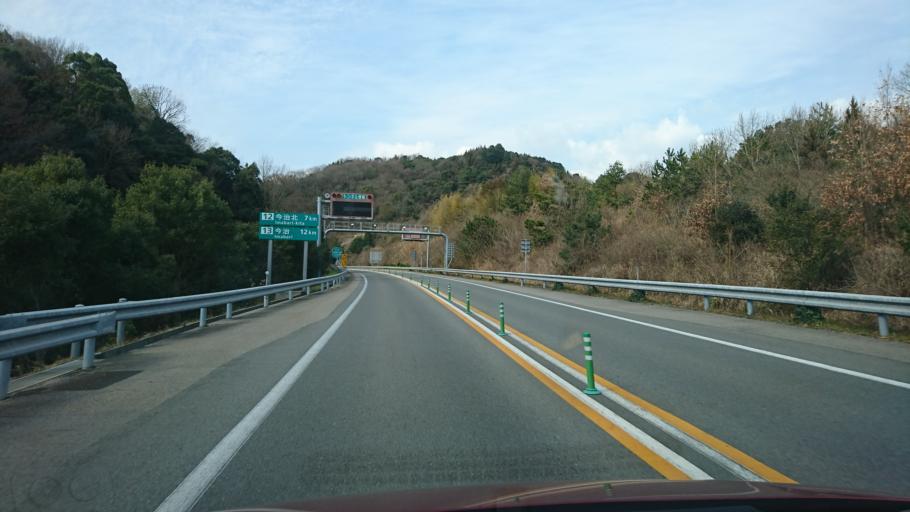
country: JP
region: Hiroshima
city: Innoshima
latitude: 34.1308
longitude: 133.0296
